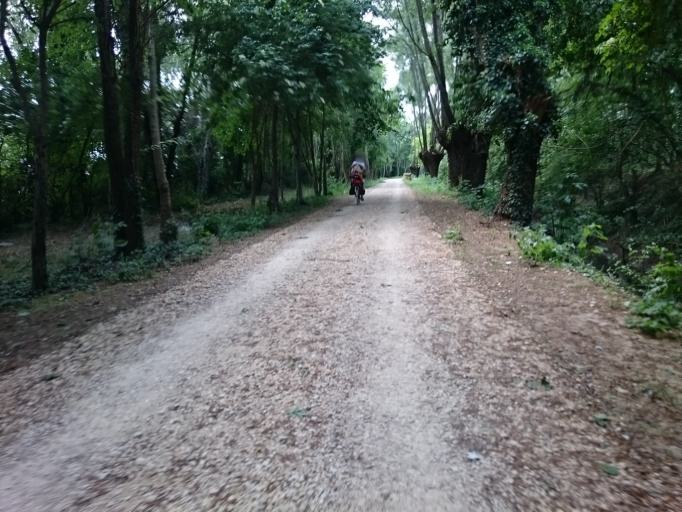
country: IT
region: Veneto
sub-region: Provincia di Padova
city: Este
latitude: 45.2161
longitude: 11.6509
